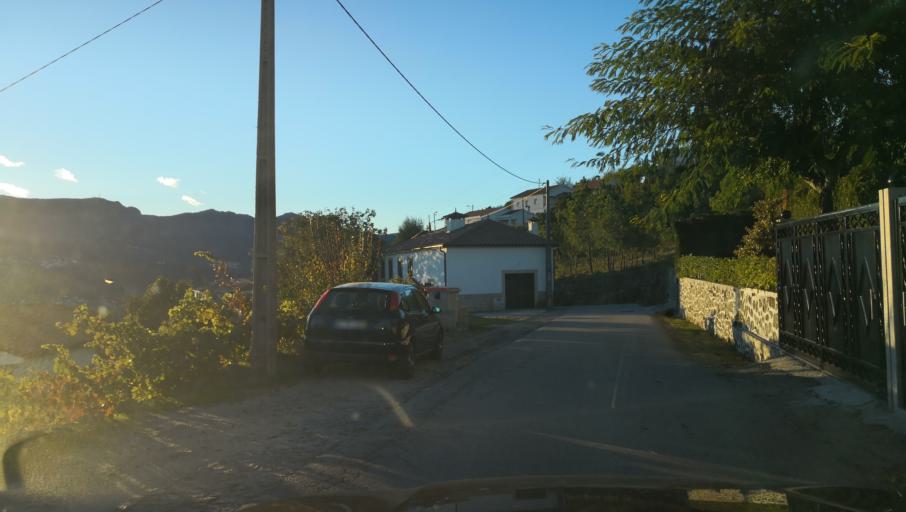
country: PT
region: Vila Real
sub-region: Santa Marta de Penaguiao
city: Santa Marta de Penaguiao
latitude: 41.2553
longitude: -7.7833
